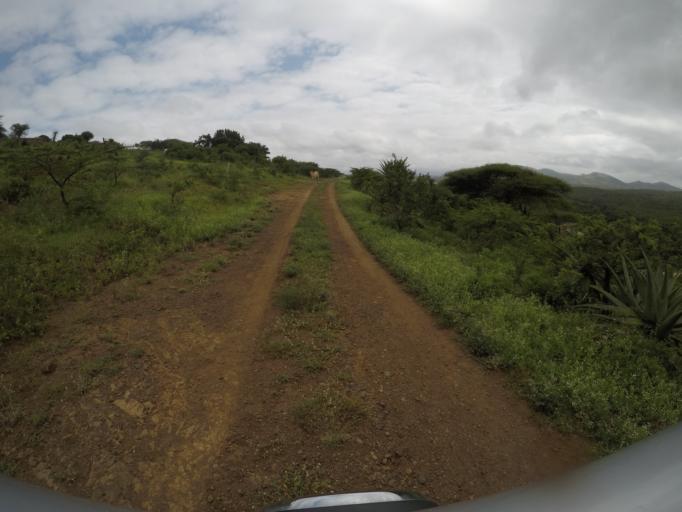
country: ZA
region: KwaZulu-Natal
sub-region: uThungulu District Municipality
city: Empangeni
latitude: -28.6272
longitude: 31.8756
